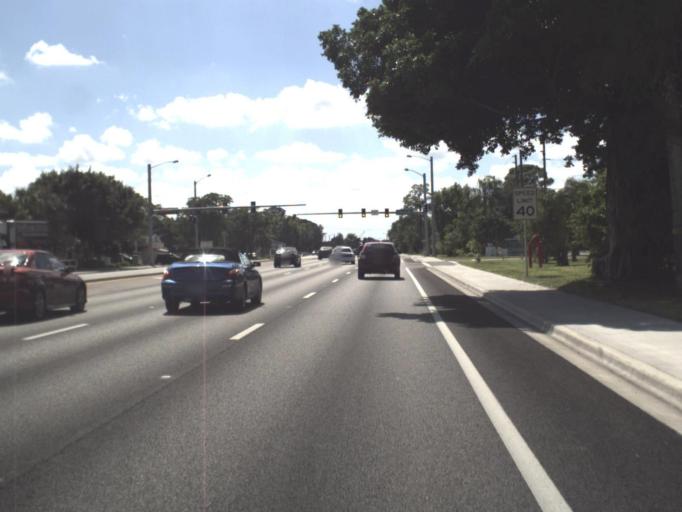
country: US
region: Florida
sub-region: Lee County
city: Estero
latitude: 26.4383
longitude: -81.8110
